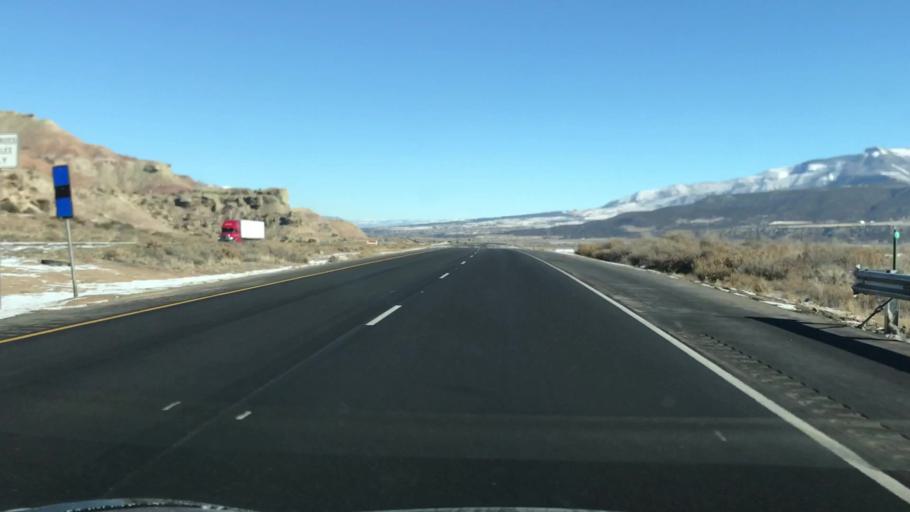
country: US
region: Colorado
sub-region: Garfield County
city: Parachute
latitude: 39.3984
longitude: -108.1188
